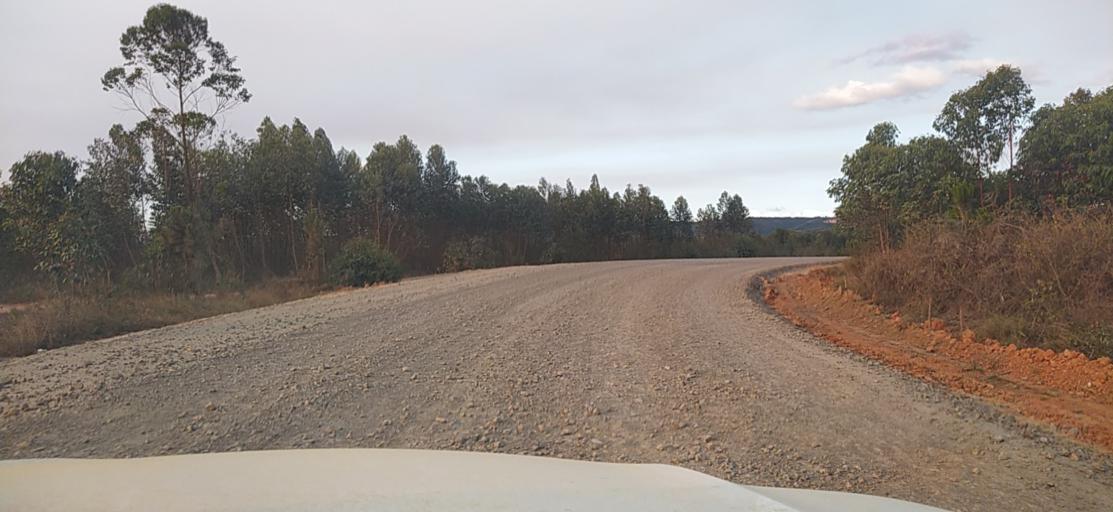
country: MG
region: Analamanga
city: Anjozorobe
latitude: -18.5058
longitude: 48.2641
